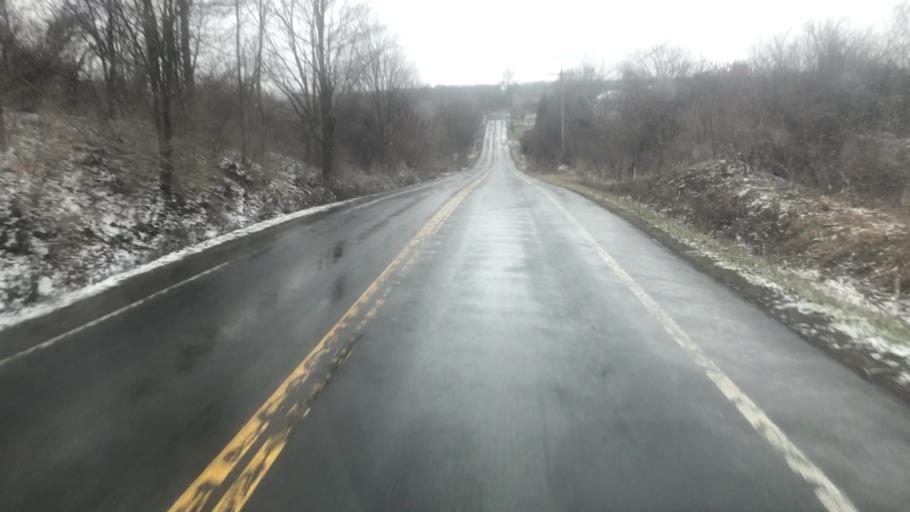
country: US
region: New York
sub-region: Onondaga County
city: Skaneateles
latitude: 42.9945
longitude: -76.3990
